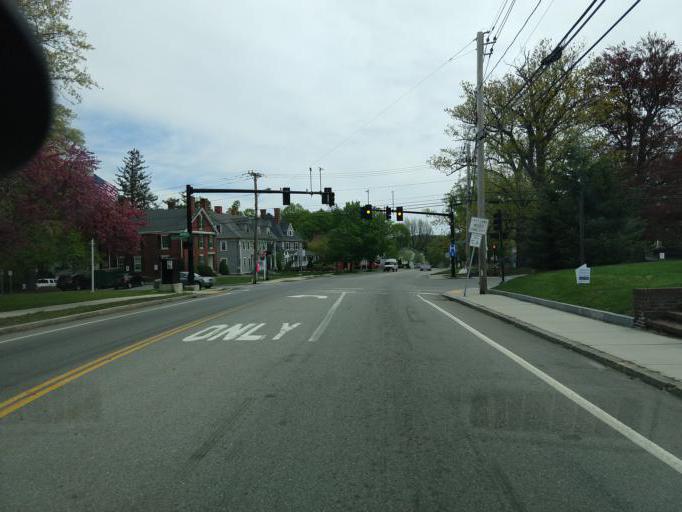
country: US
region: Massachusetts
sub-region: Essex County
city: Haverhill
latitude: 42.7661
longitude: -71.0811
